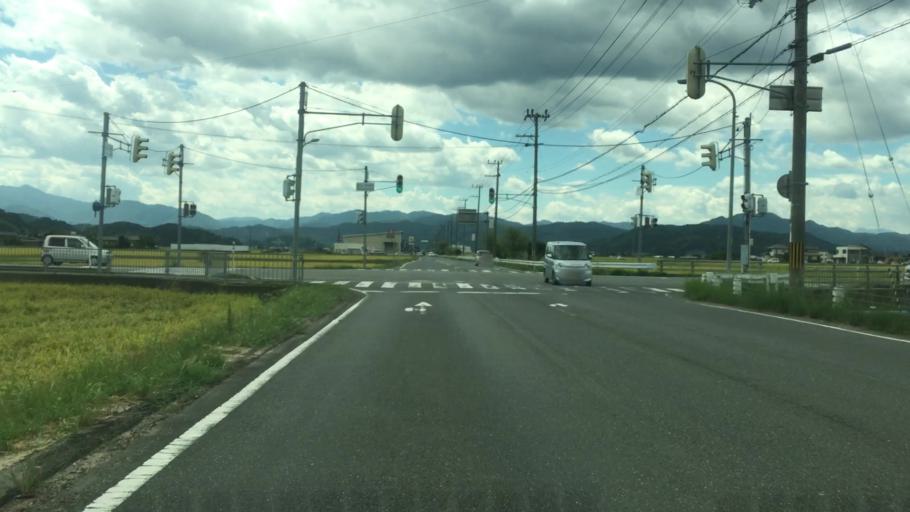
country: JP
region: Hyogo
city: Toyooka
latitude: 35.5281
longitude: 134.8398
